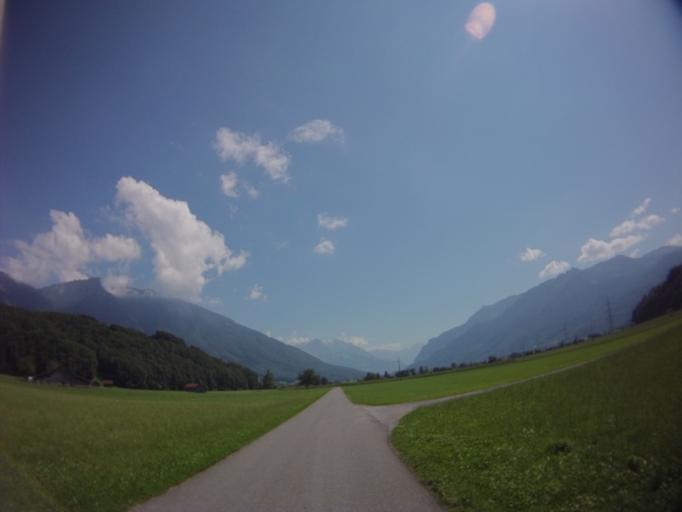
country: CH
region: Saint Gallen
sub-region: Wahlkreis See-Gaster
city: Kaltbrunn
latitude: 47.1963
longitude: 9.0317
